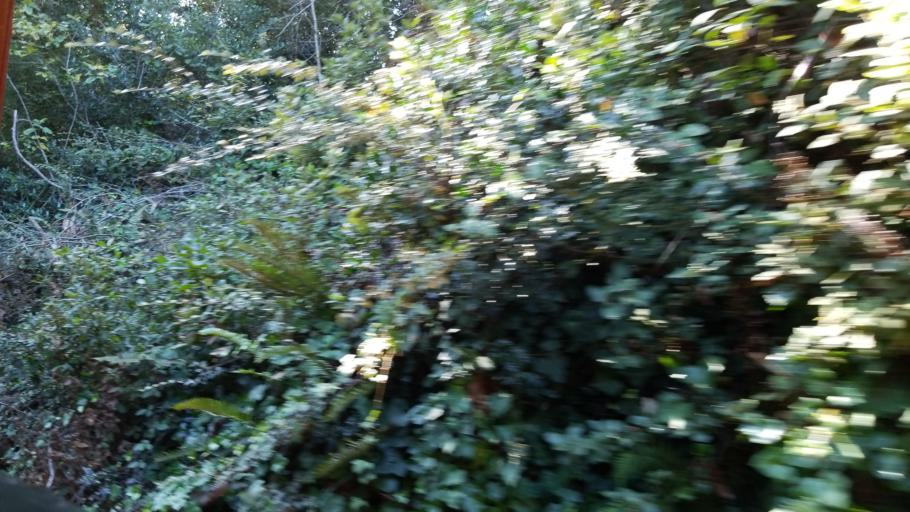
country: US
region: California
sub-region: Mendocino County
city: Fort Bragg
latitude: 39.4492
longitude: -123.7974
